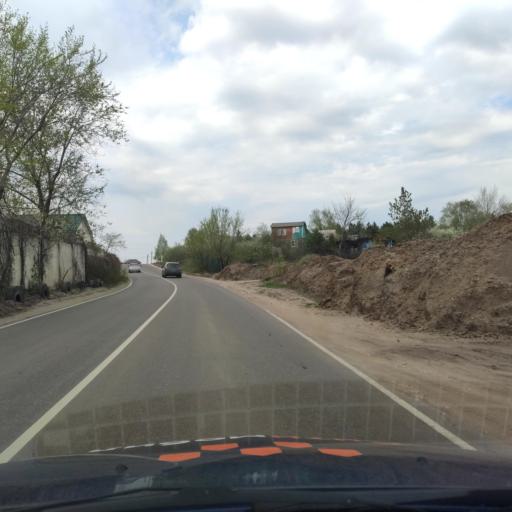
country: RU
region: Voronezj
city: Podgornoye
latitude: 51.8376
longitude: 39.1438
